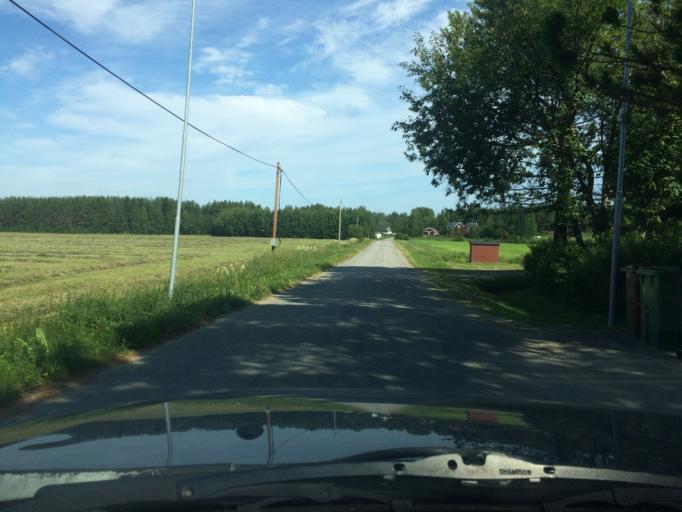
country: SE
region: Norrbotten
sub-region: Pitea Kommun
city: Bergsviken
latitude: 65.3546
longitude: 21.4148
